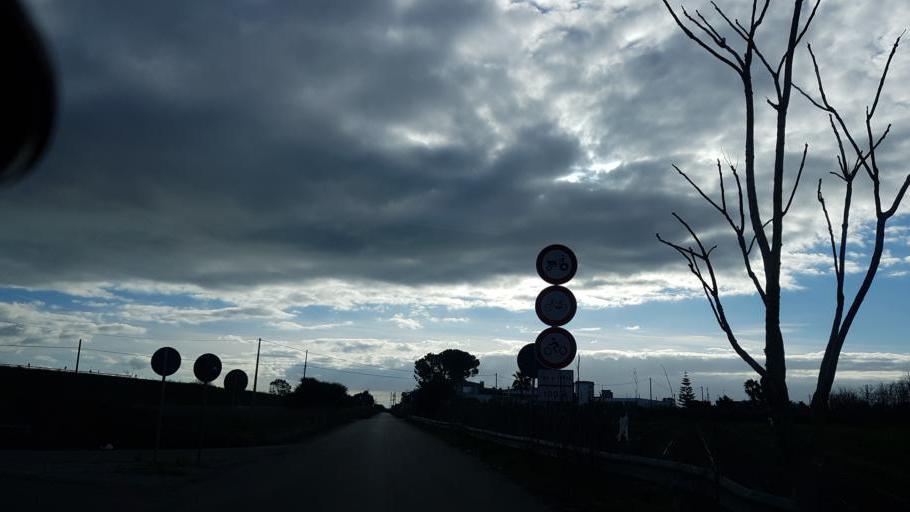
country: IT
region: Apulia
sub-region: Provincia di Brindisi
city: La Rosa
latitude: 40.6166
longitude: 17.9527
